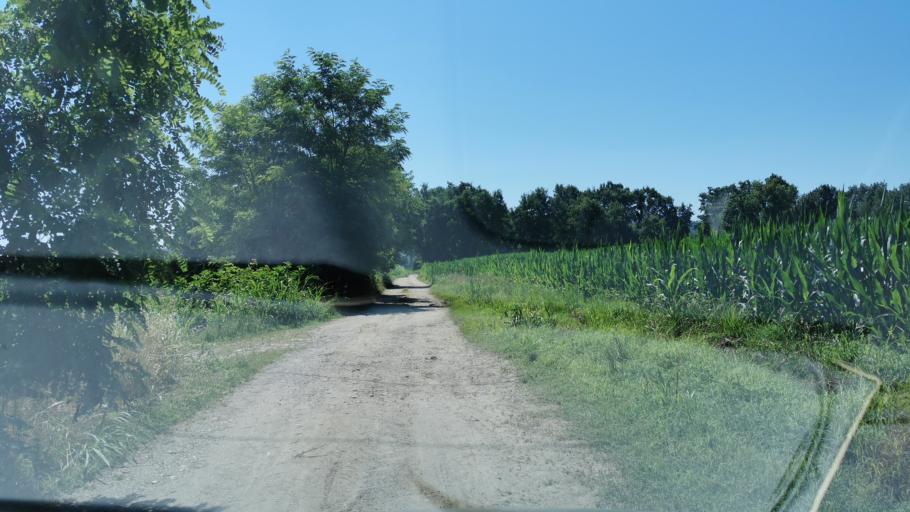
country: IT
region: Piedmont
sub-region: Provincia di Torino
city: Brandizzo
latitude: 45.1900
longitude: 7.8353
